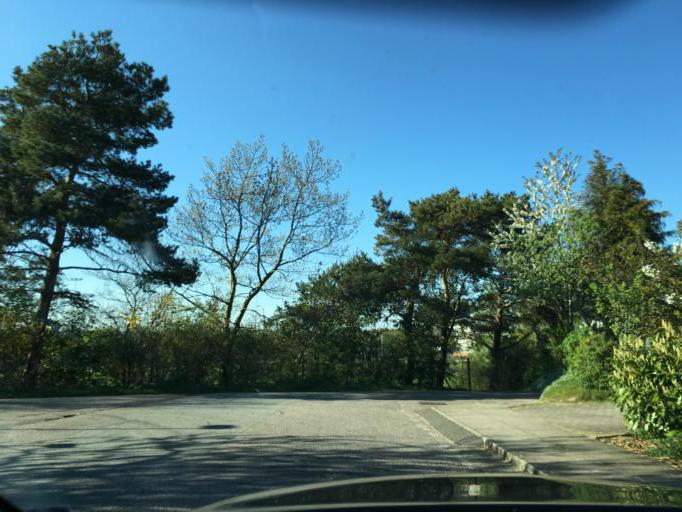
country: DK
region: South Denmark
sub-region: Kolding Kommune
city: Kolding
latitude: 55.5264
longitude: 9.4702
